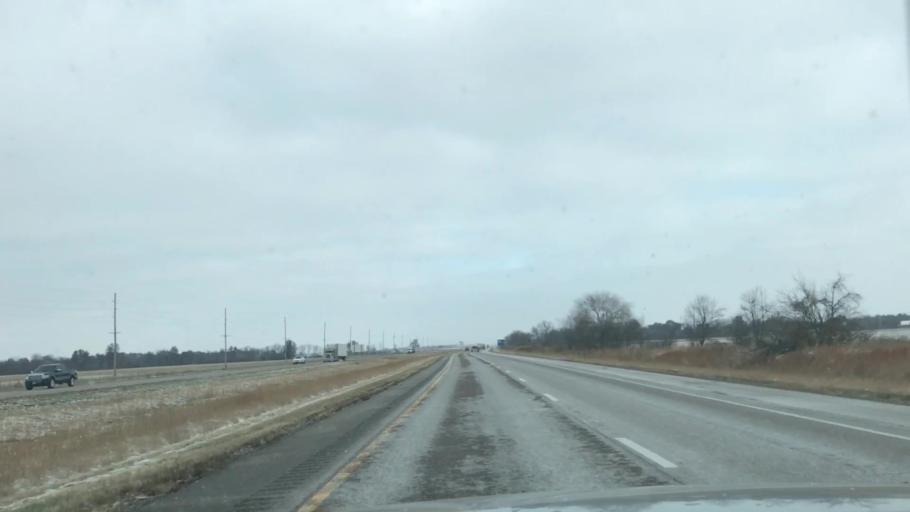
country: US
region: Illinois
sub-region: Macoupin County
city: Staunton
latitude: 38.9833
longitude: -89.7493
